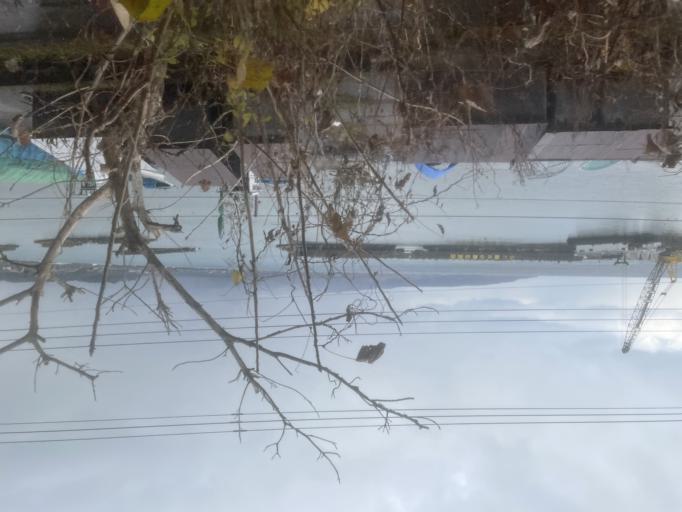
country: JP
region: Aomori
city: Shimokizukuri
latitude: 41.1843
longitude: 140.4602
